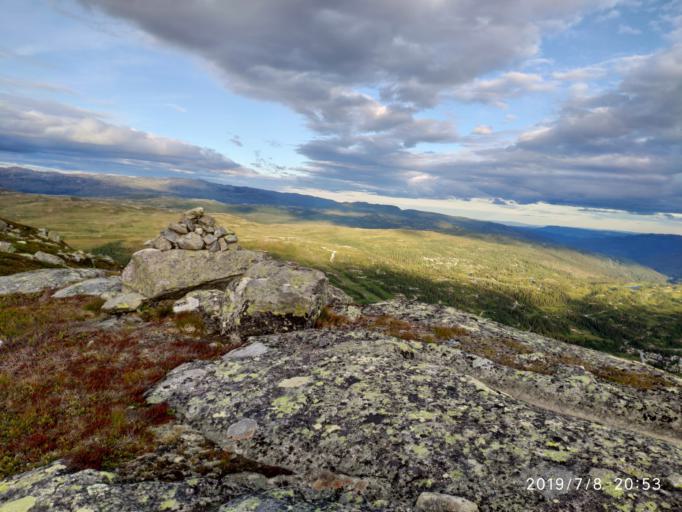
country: NO
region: Buskerud
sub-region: Nes
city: Nesbyen
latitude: 60.3558
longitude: 9.1749
